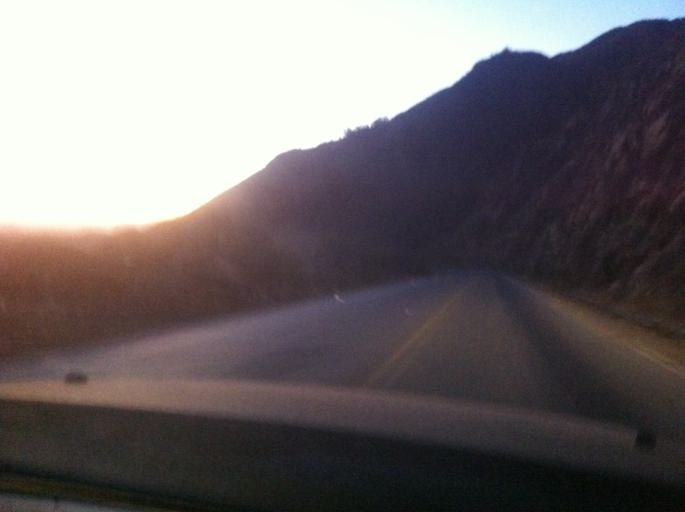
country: BO
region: Cochabamba
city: Irpa Irpa
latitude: -17.6634
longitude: -66.4493
